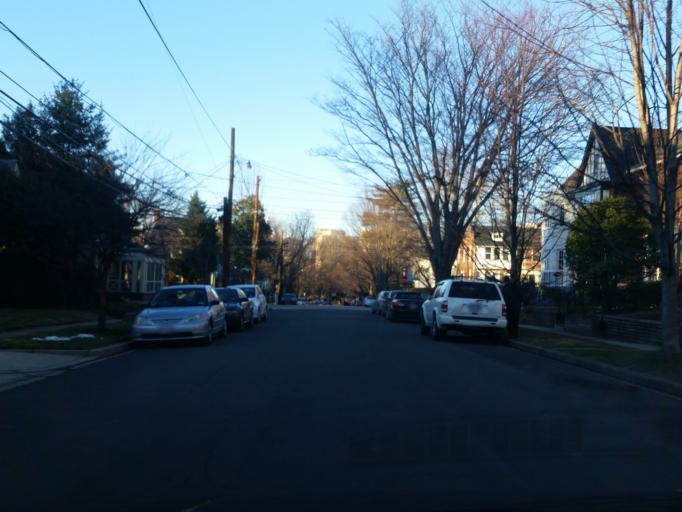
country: US
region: Maryland
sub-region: Montgomery County
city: Friendship Village
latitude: 38.9564
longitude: -77.0886
